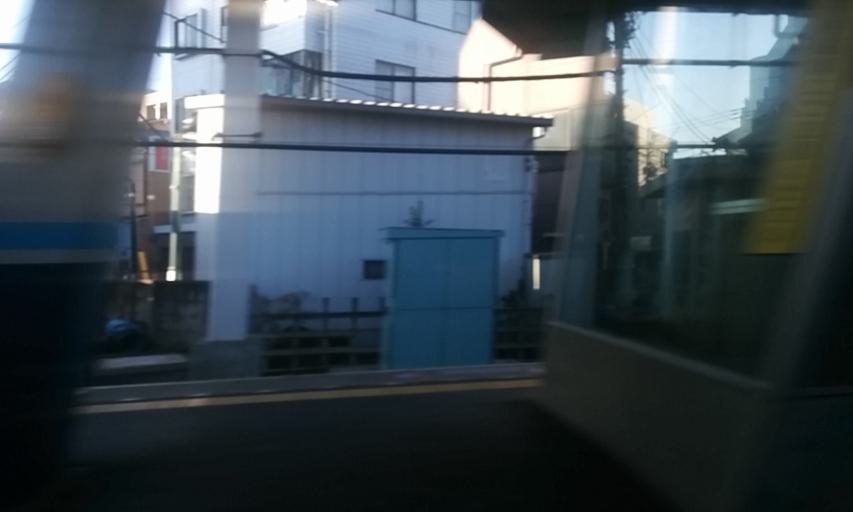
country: JP
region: Saitama
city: Kawaguchi
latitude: 35.7559
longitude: 139.6952
